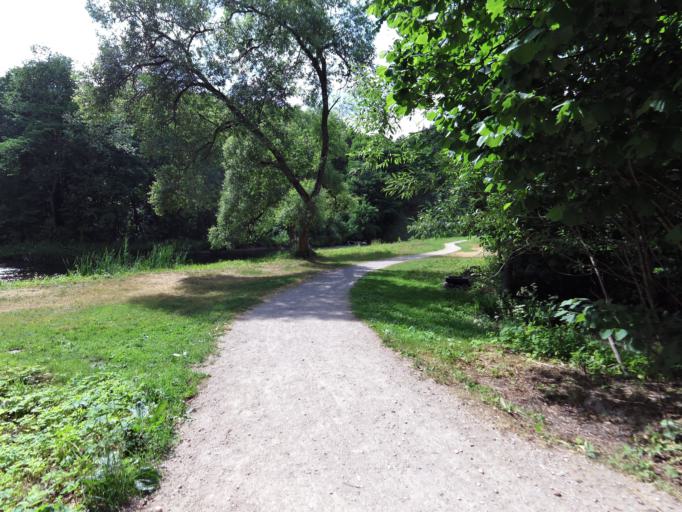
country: LT
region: Vilnius County
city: Rasos
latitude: 54.6891
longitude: 25.3541
